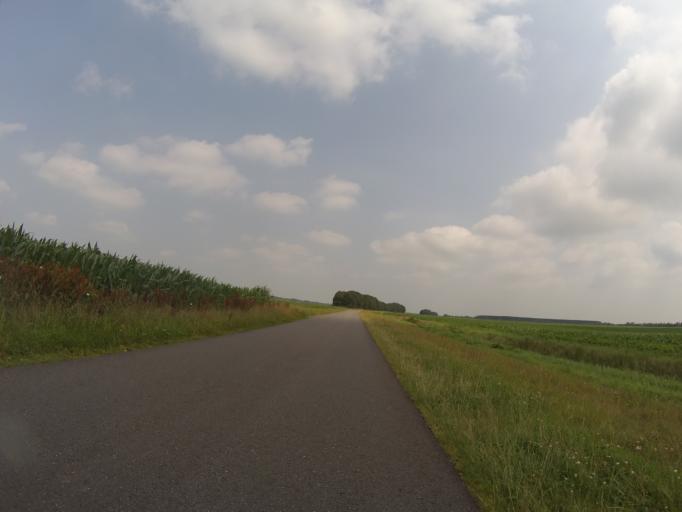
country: NL
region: Drenthe
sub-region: Gemeente Emmen
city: Emmen
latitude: 52.8576
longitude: 6.9473
